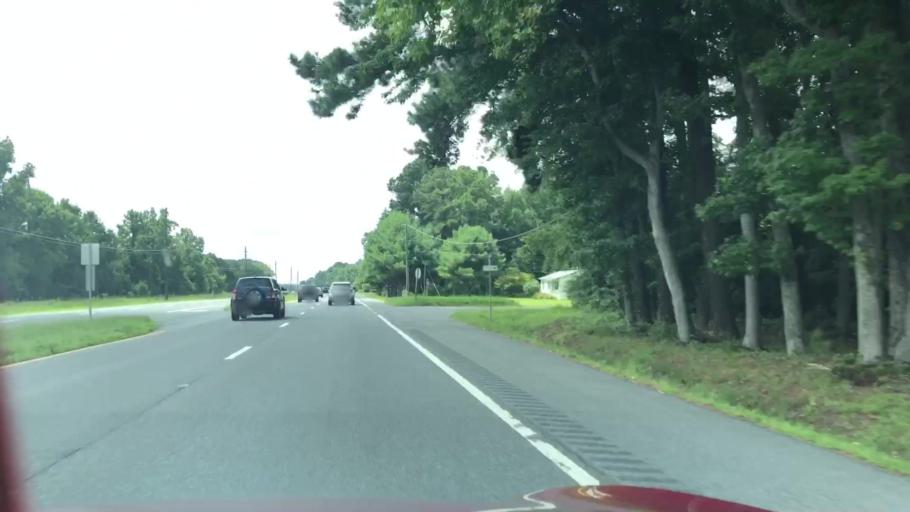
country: US
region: Virginia
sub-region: Northampton County
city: Eastville
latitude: 37.4247
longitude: -75.8921
